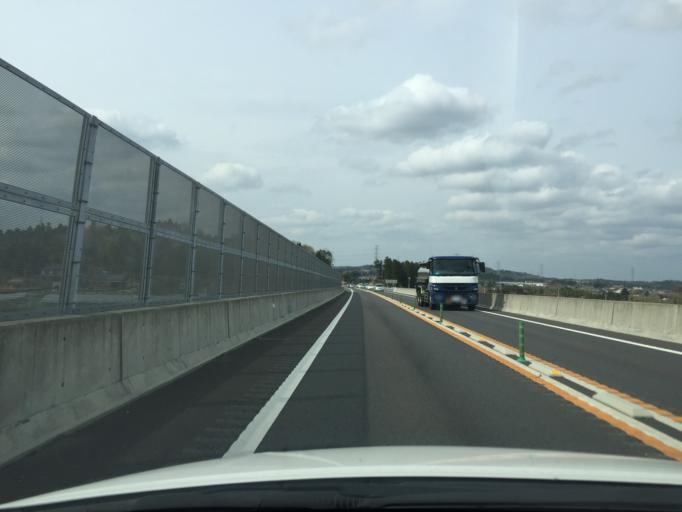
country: JP
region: Fukushima
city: Namie
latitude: 37.3895
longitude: 140.9667
